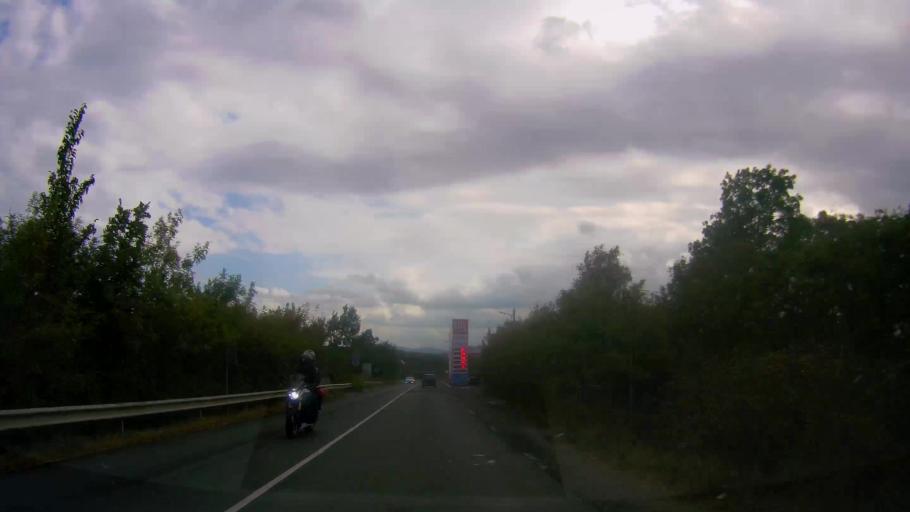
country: BG
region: Burgas
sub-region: Obshtina Primorsko
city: Primorsko
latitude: 42.2691
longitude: 27.7424
